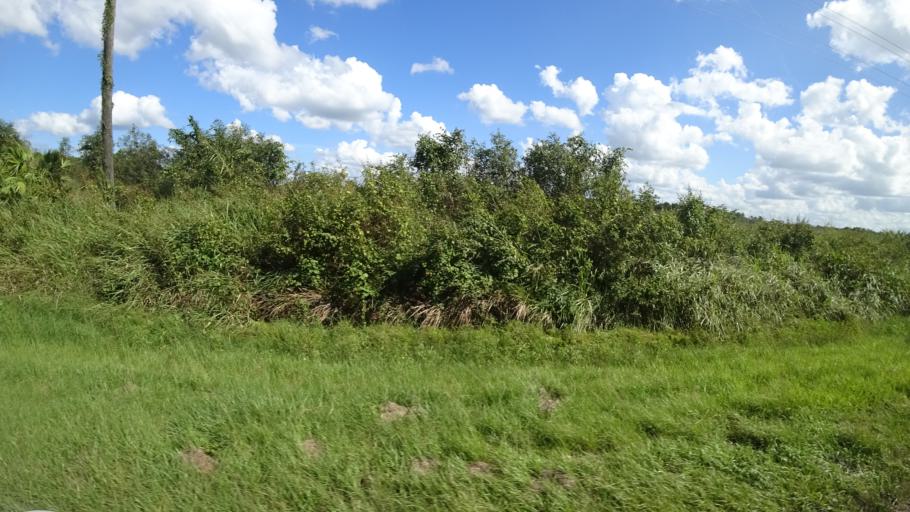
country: US
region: Florida
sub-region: Sarasota County
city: Lake Sarasota
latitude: 27.3800
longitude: -82.1397
